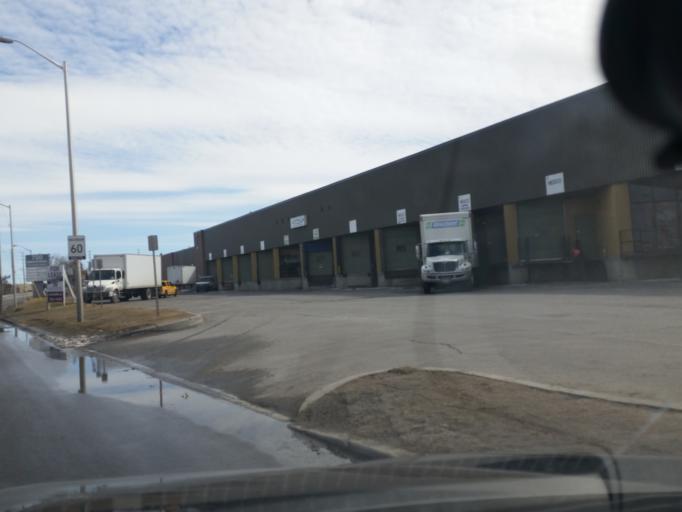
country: CA
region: Ontario
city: Ottawa
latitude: 45.4104
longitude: -75.6400
